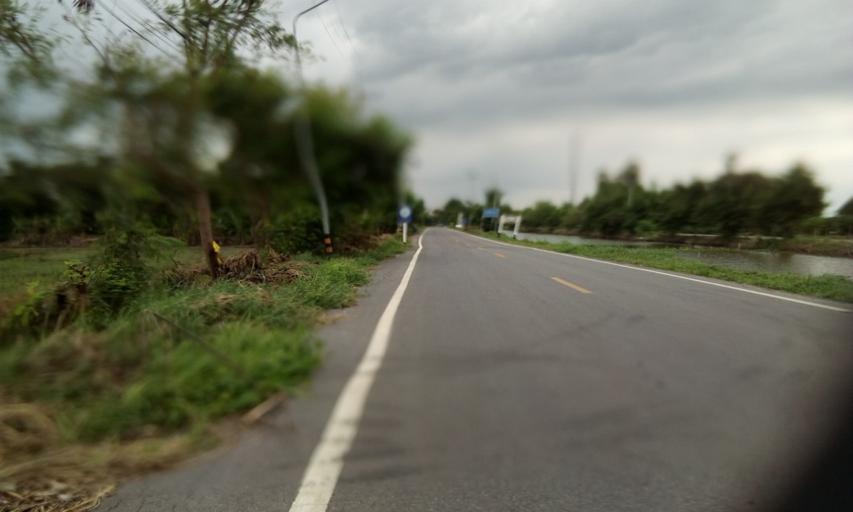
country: TH
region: Pathum Thani
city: Nong Suea
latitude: 14.0749
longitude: 100.8462
